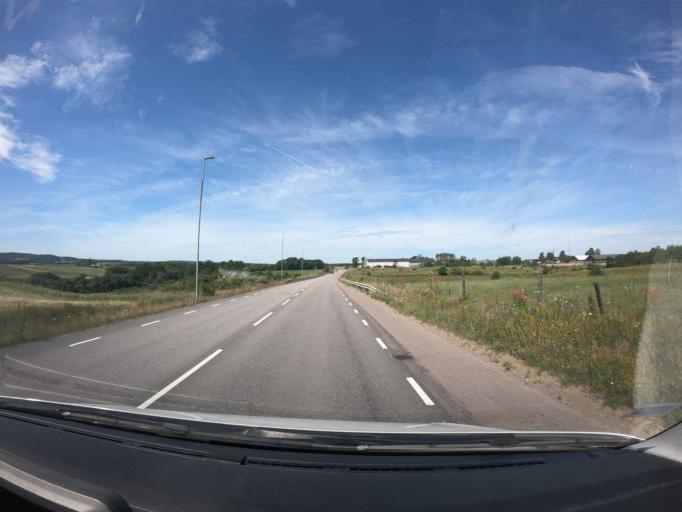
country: SE
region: Skane
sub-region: Klippans Kommun
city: Klippan
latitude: 56.1287
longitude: 13.1190
